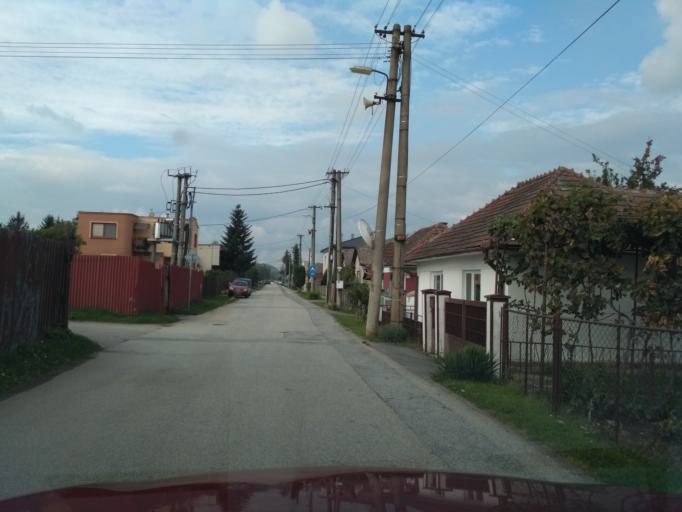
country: SK
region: Kosicky
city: Kosice
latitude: 48.6376
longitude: 21.1691
